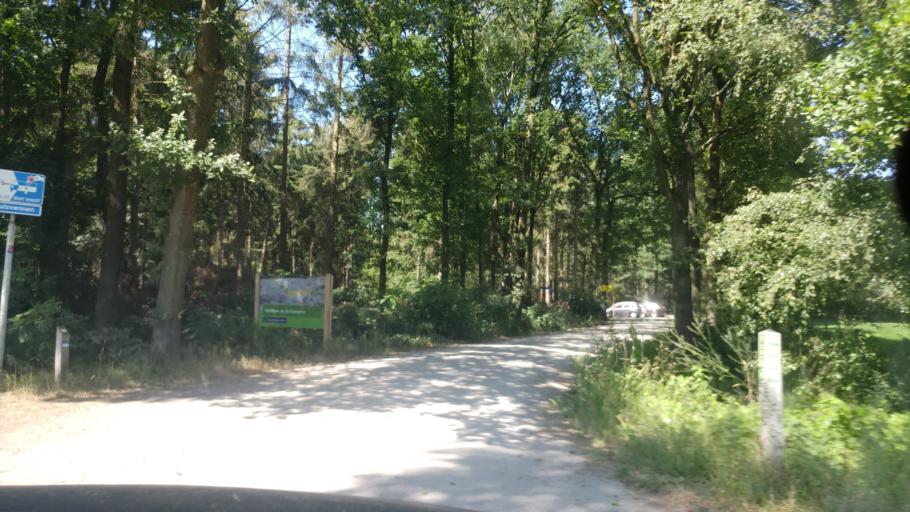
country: NL
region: North Brabant
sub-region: Gemeente Boxtel
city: Boxtel
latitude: 51.5805
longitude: 5.2828
